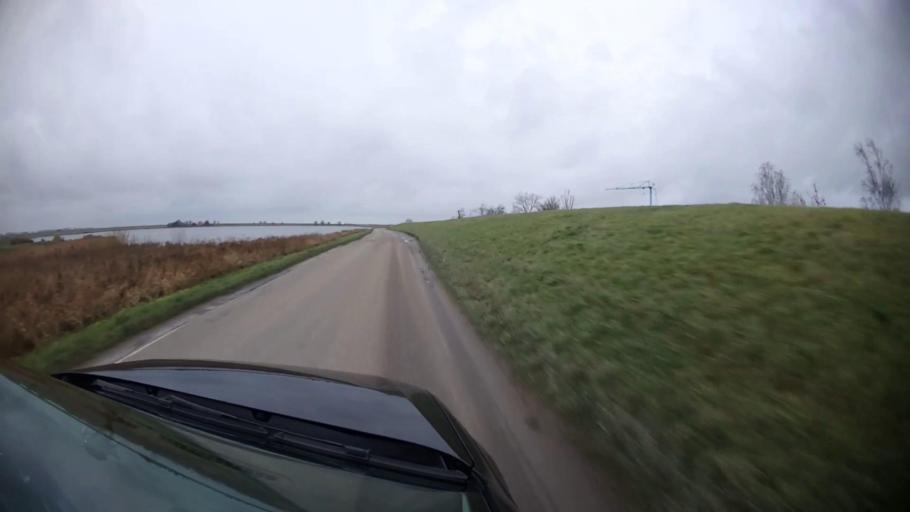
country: NL
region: North Holland
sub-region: Gemeente Waterland
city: Marken
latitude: 52.4300
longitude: 5.0718
